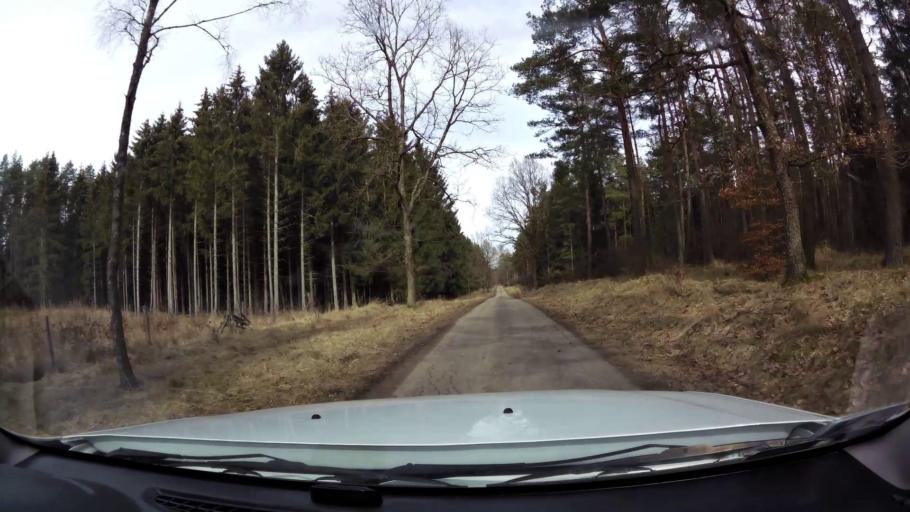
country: PL
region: West Pomeranian Voivodeship
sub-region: Powiat drawski
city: Drawsko Pomorskie
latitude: 53.4861
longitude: 15.7002
